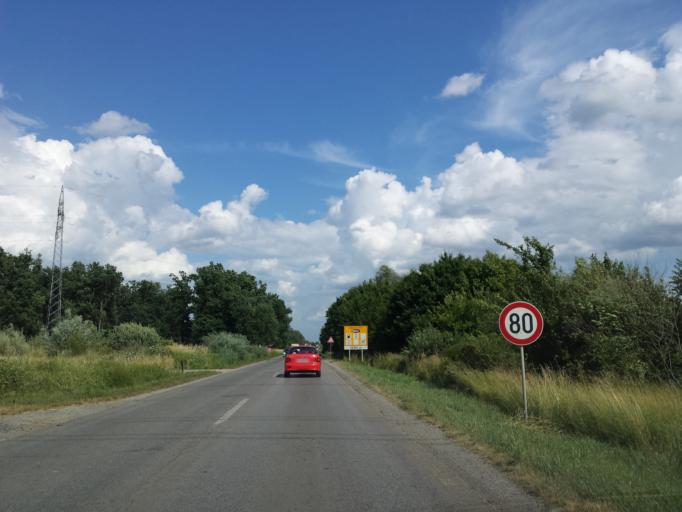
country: HR
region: Grad Zagreb
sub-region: Sesvete
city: Sesvete
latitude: 45.8132
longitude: 16.1900
